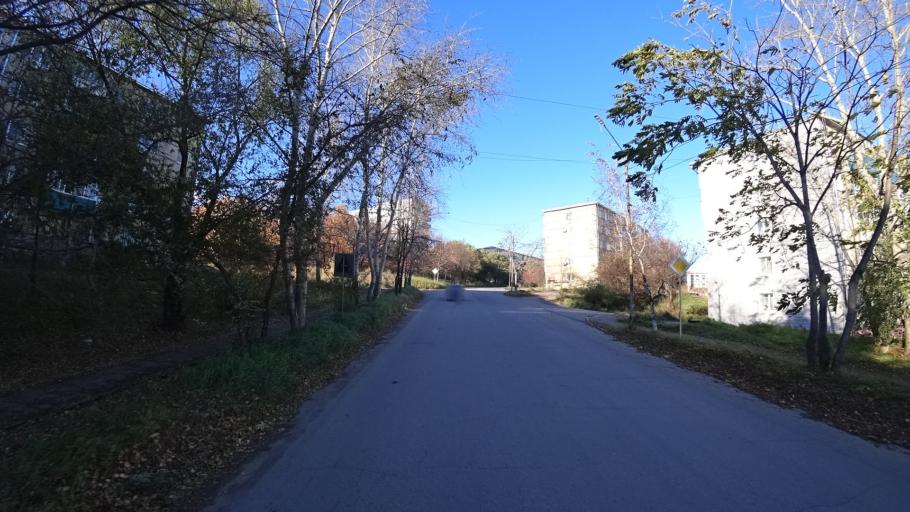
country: RU
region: Khabarovsk Krai
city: Amursk
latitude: 50.2402
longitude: 136.9048
